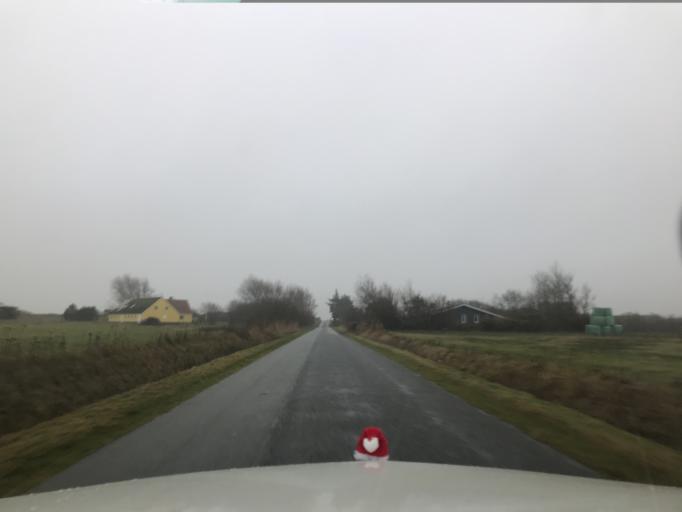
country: DK
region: South Denmark
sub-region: Esbjerg Kommune
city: Tjaereborg
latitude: 55.2824
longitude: 8.5517
